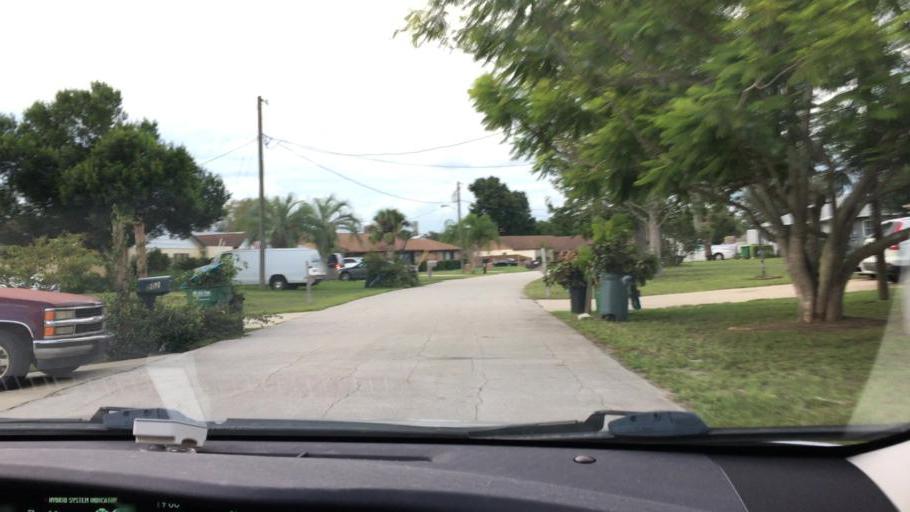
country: US
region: Florida
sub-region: Volusia County
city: Deltona
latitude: 28.8764
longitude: -81.2382
